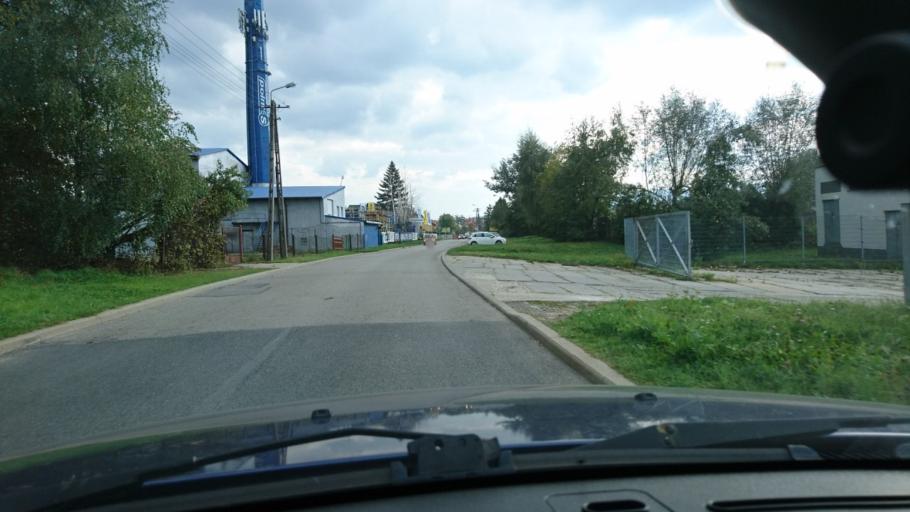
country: PL
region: Silesian Voivodeship
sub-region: Bielsko-Biala
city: Bielsko-Biala
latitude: 49.8444
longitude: 19.0555
